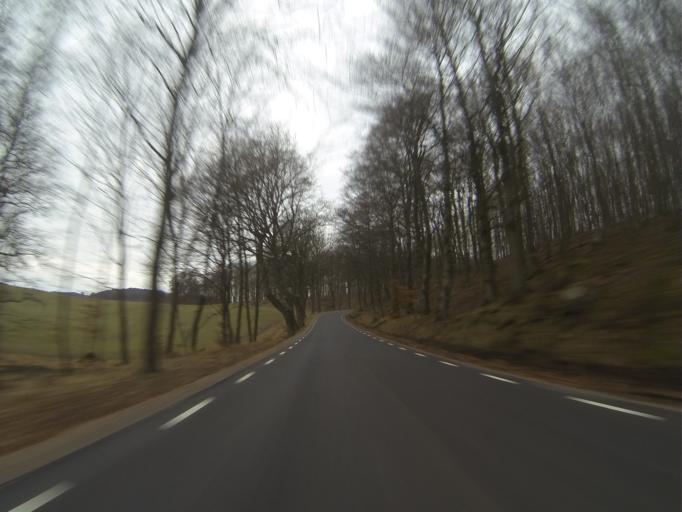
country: SE
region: Skane
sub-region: Lunds Kommun
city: Genarp
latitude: 55.5728
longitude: 13.4320
